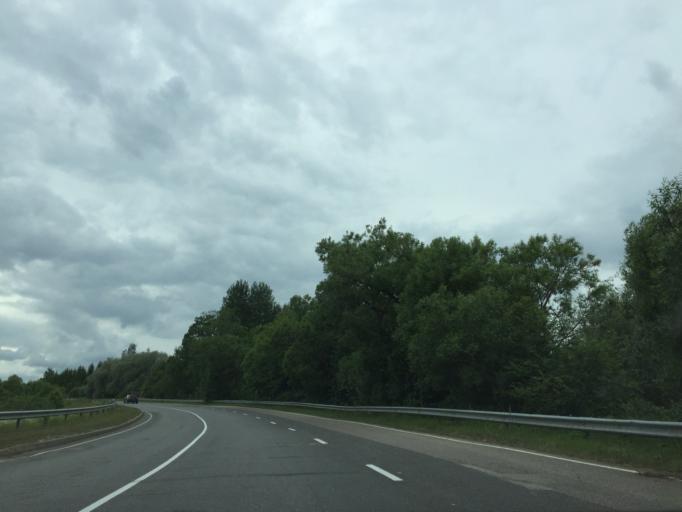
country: LV
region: Apes Novads
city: Ape
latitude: 57.4549
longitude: 26.3473
